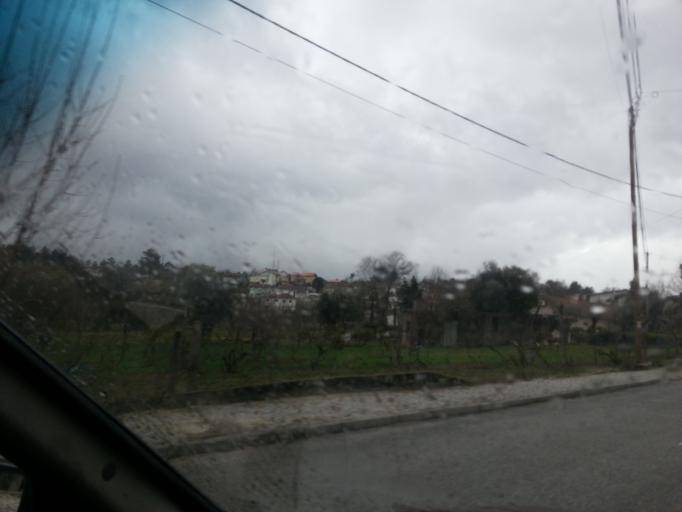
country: PT
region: Viseu
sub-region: Viseu
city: Rio de Loba
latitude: 40.6675
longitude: -7.8789
